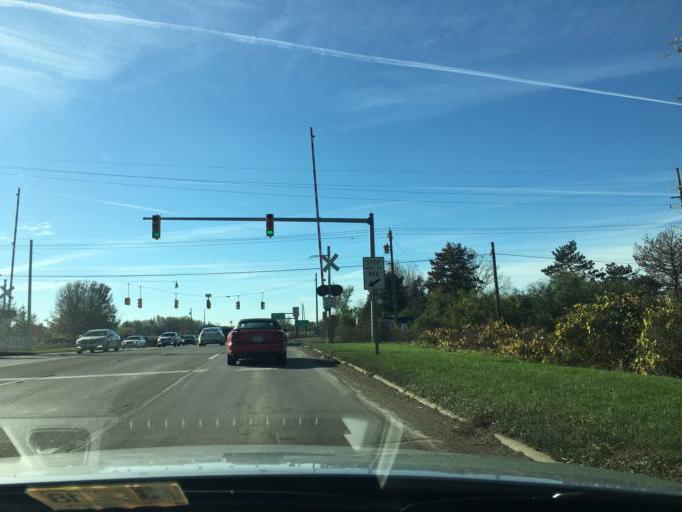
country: US
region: Michigan
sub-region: Wayne County
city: Plymouth
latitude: 42.3866
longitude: -83.5100
